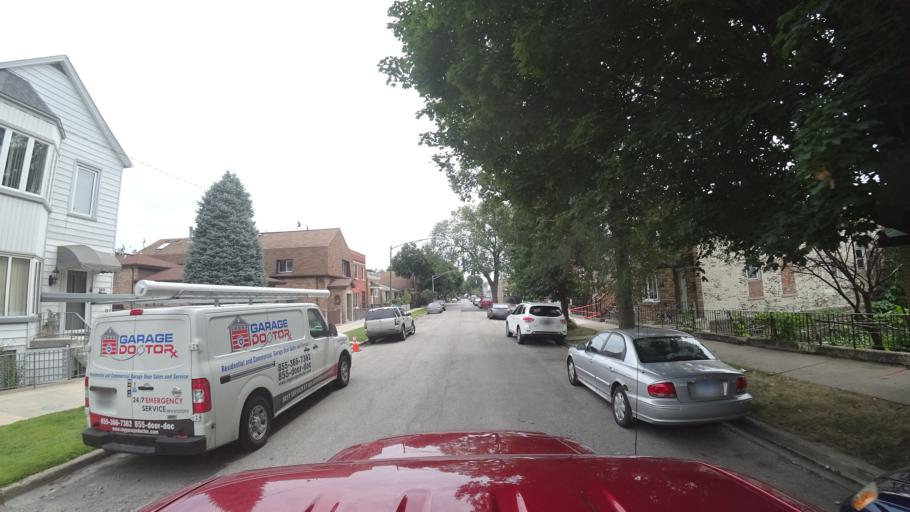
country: US
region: Illinois
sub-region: Cook County
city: Chicago
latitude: 41.8402
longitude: -87.6576
